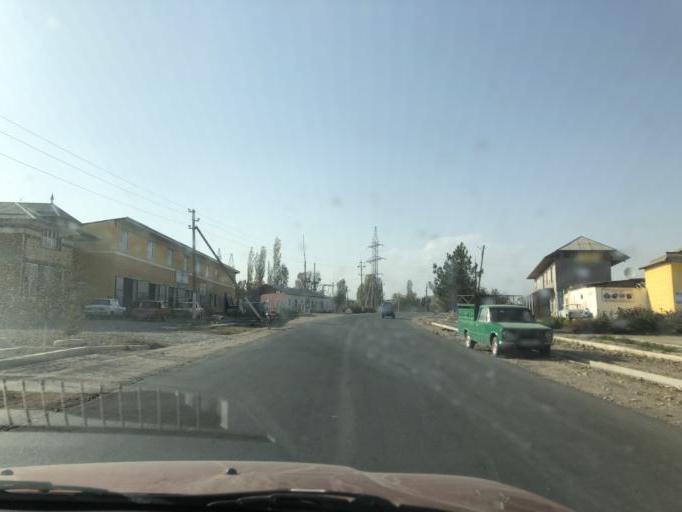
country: UZ
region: Namangan
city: Chust Shahri
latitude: 41.0740
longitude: 71.2011
